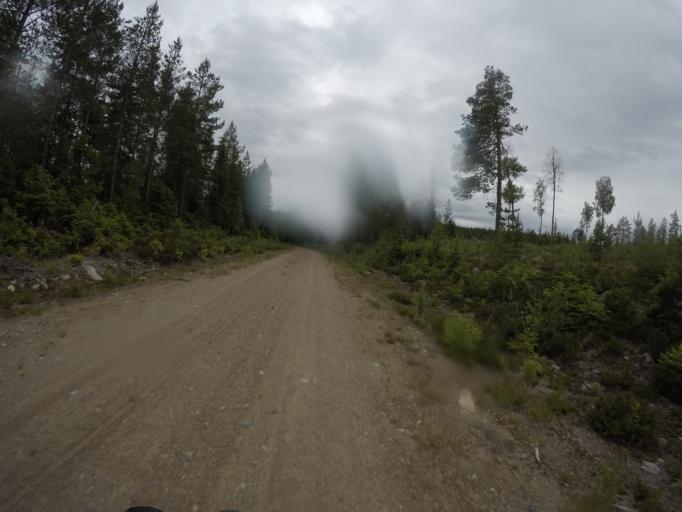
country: SE
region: Dalarna
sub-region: Ludvika Kommun
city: Abborrberget
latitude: 60.0508
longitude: 14.5797
